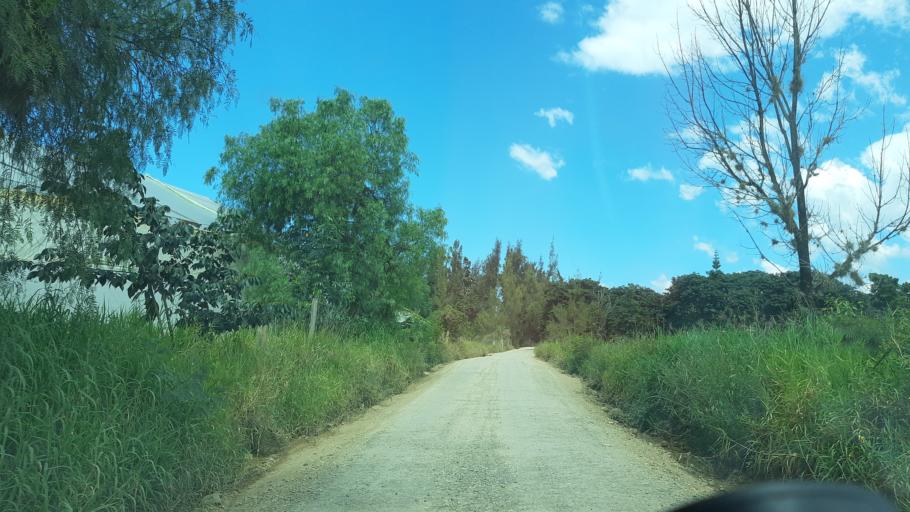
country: CO
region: Boyaca
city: Villa de Leiva
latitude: 5.6597
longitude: -73.5728
